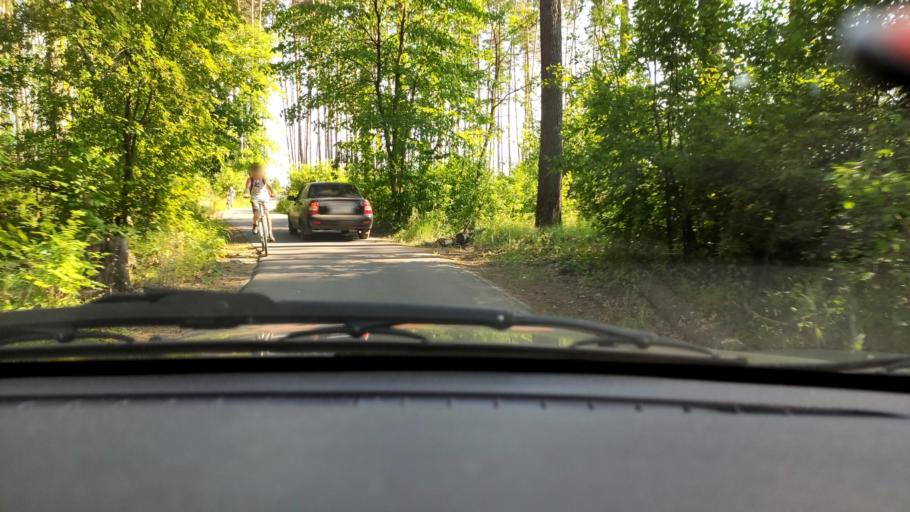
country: RU
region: Voronezj
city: Somovo
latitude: 51.7913
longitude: 39.3810
